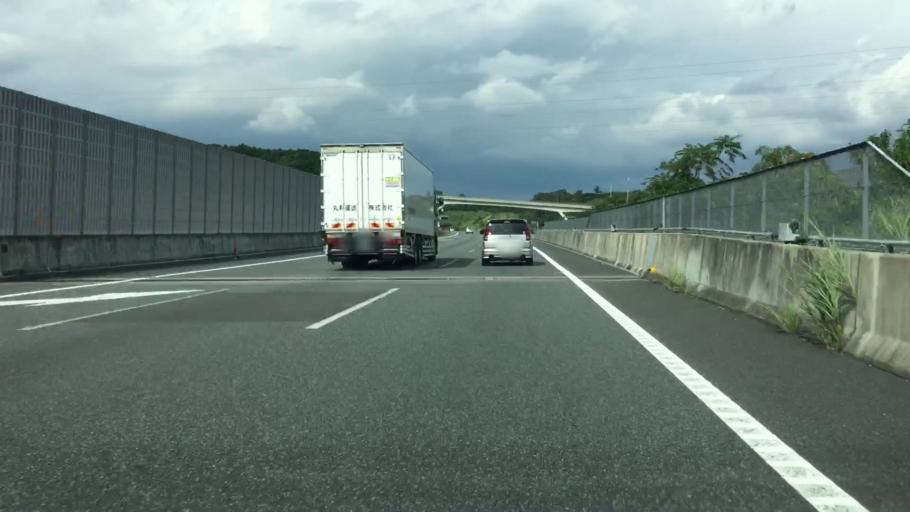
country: JP
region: Shizuoka
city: Mishima
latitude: 35.1702
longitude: 138.8824
